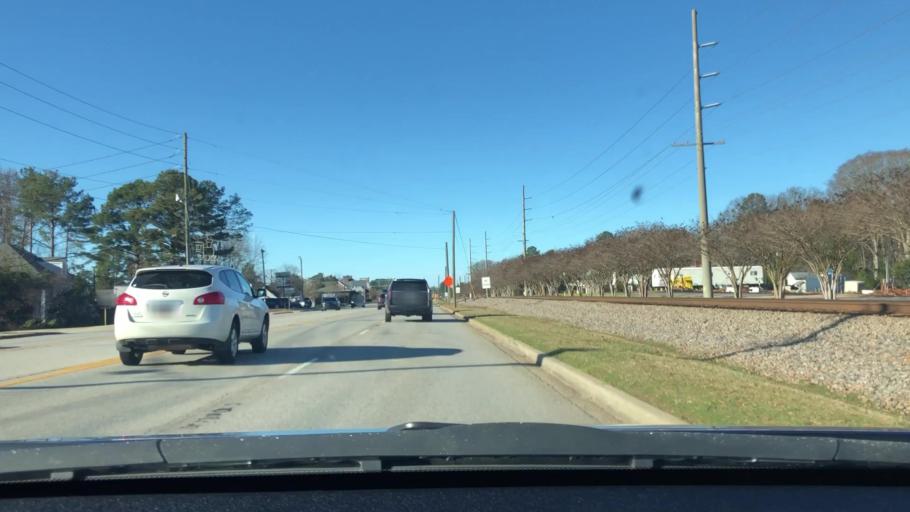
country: US
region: South Carolina
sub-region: Lexington County
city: Irmo
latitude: 34.0802
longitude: -81.1801
